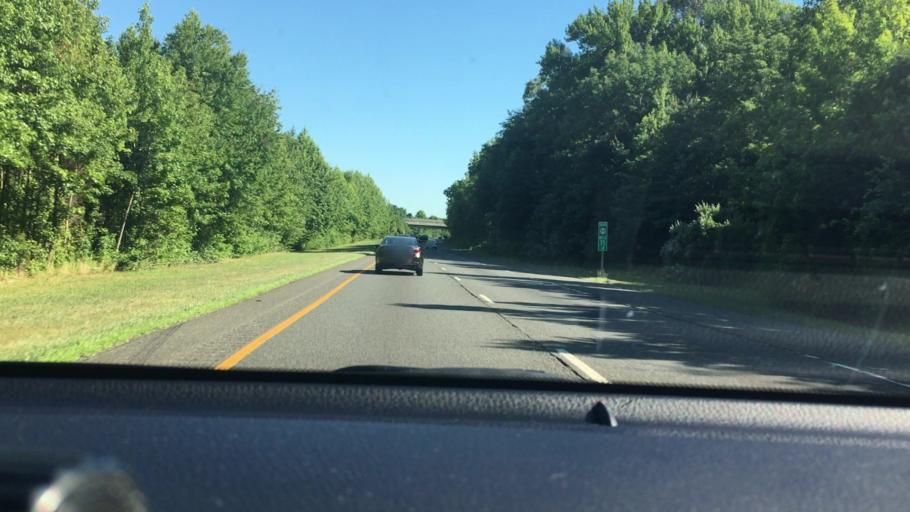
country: US
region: New Jersey
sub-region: Gloucester County
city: Wenonah
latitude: 39.7819
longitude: -75.1163
